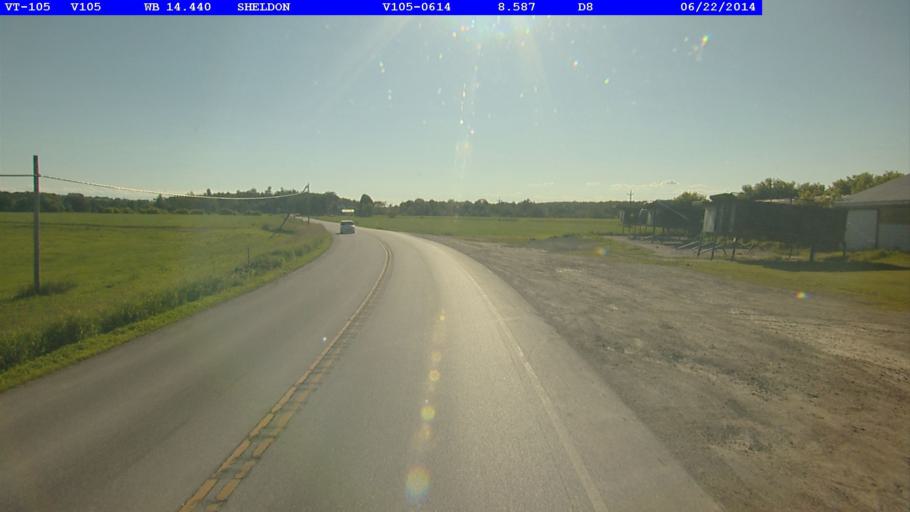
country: US
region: Vermont
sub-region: Franklin County
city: Enosburg Falls
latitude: 44.9113
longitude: -72.8681
